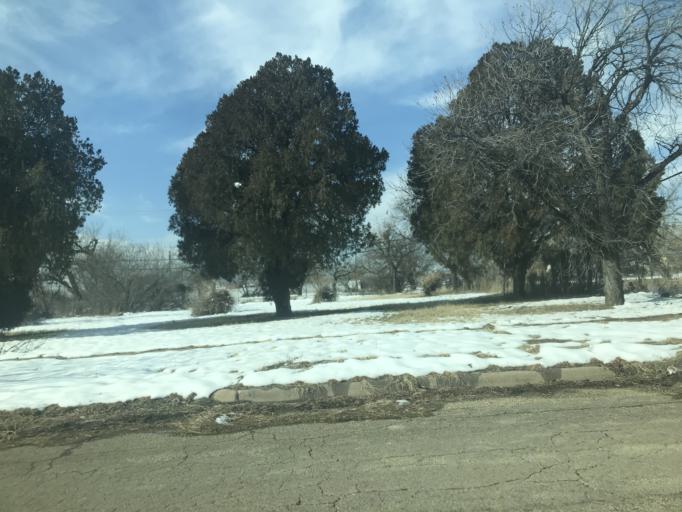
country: US
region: Texas
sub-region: Taylor County
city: Abilene
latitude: 32.4631
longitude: -99.7278
